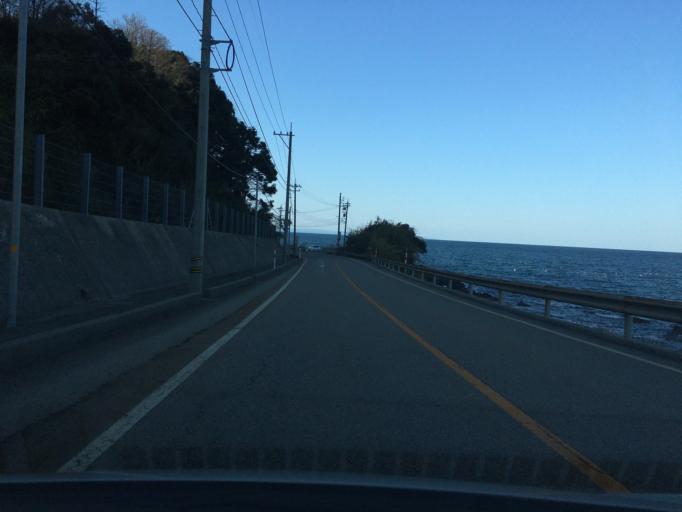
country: JP
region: Ishikawa
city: Nanao
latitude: 36.9933
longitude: 137.0530
